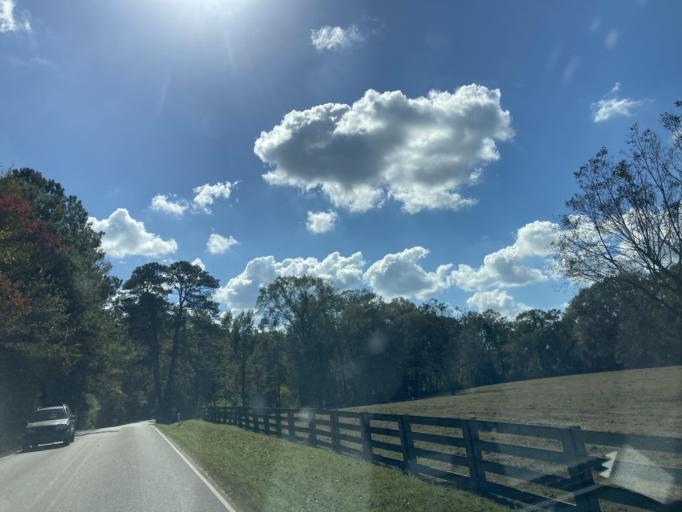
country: US
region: Mississippi
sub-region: Lamar County
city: West Hattiesburg
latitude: 31.2534
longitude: -89.4349
